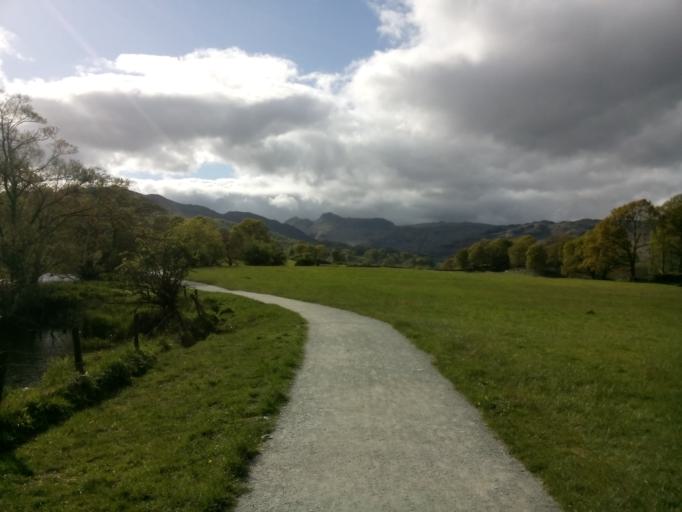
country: GB
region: England
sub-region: Cumbria
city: Ambleside
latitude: 54.4227
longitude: -3.0184
